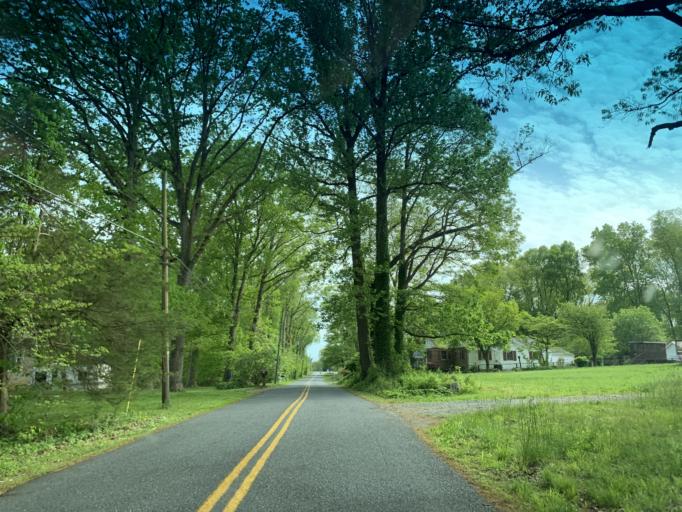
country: US
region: Maryland
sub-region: Harford County
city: Aberdeen
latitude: 39.6509
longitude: -76.2281
